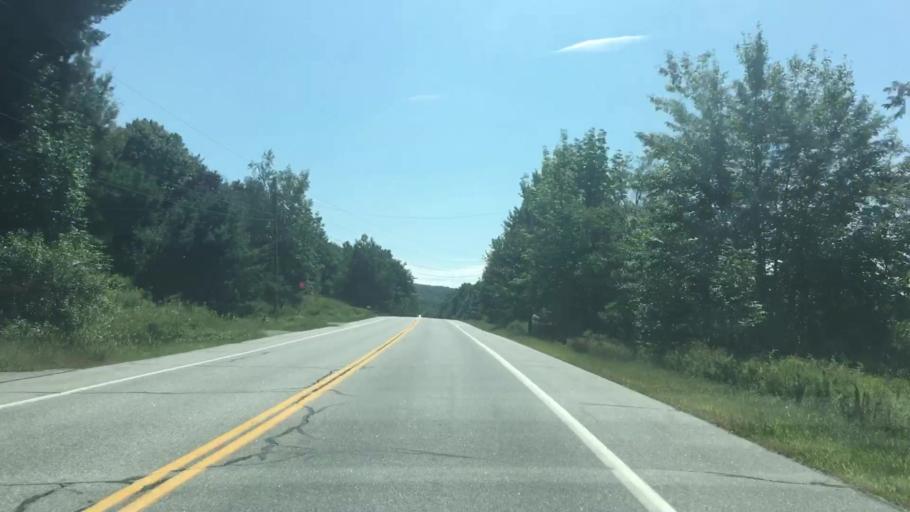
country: US
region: Maine
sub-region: Kennebec County
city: Monmouth
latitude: 44.1575
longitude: -70.0345
